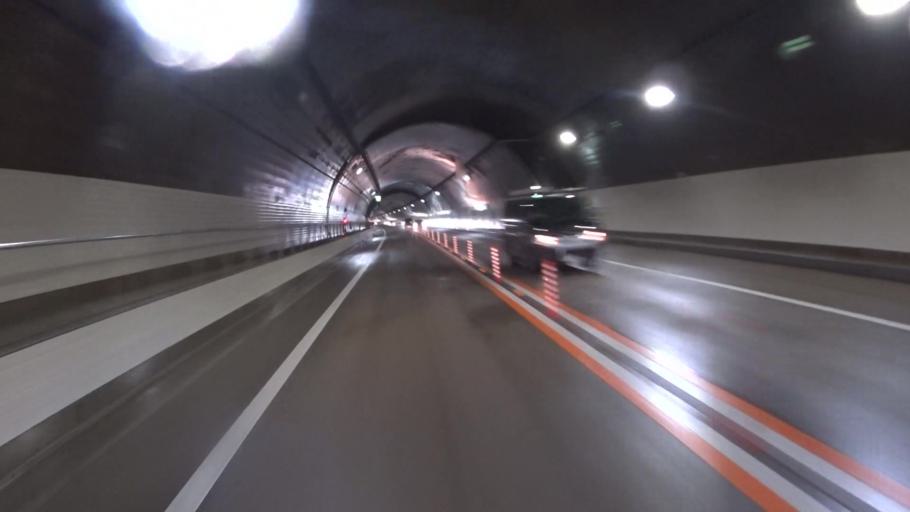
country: JP
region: Kyoto
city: Ayabe
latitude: 35.2528
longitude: 135.3417
